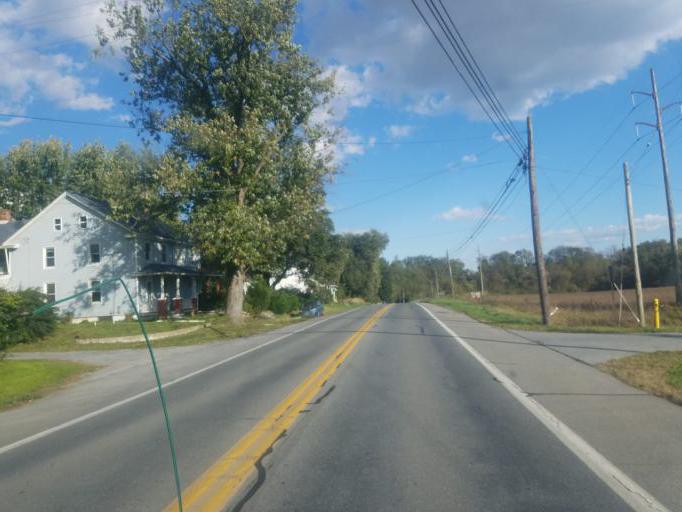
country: US
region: Pennsylvania
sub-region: Lancaster County
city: Bainbridge
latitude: 40.0777
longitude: -76.6499
